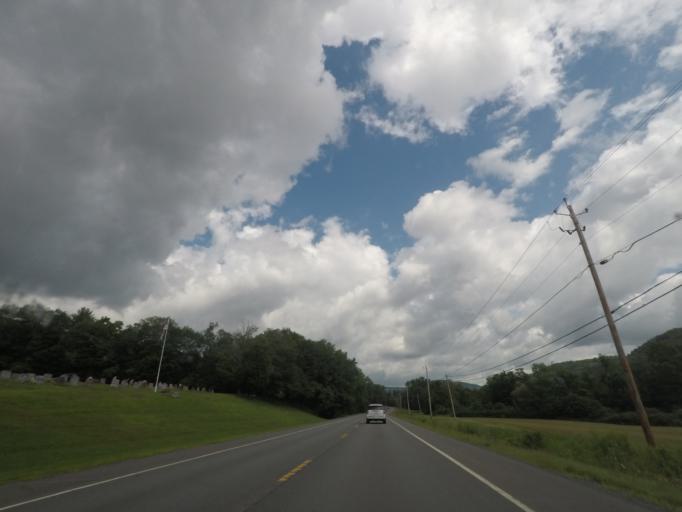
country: US
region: Massachusetts
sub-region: Berkshire County
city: Williamstown
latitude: 42.6686
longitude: -73.3697
